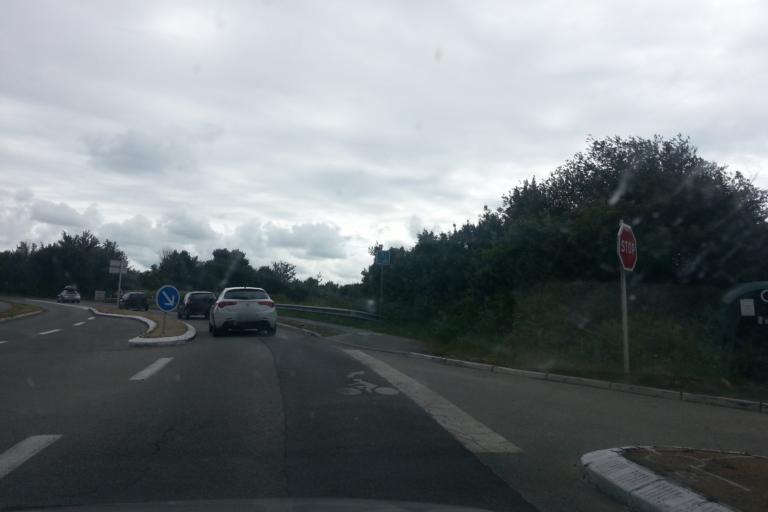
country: FR
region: Brittany
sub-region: Departement du Morbihan
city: Etel
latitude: 47.6604
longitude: -3.1850
